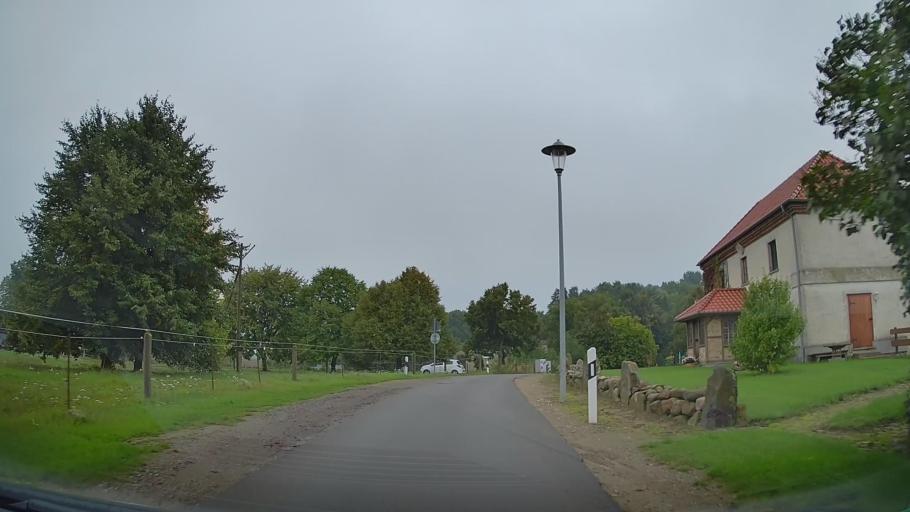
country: DE
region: Mecklenburg-Vorpommern
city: Gramkow
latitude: 53.9263
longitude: 11.3597
